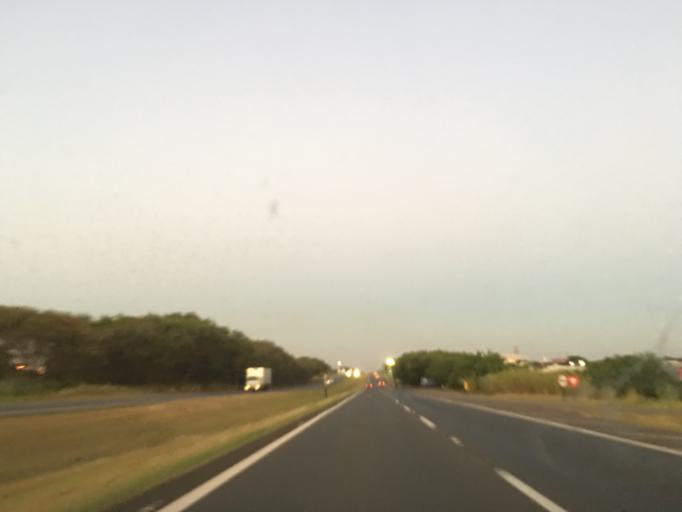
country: BR
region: Sao Paulo
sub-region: Piracicaba
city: Piracicaba
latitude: -22.7219
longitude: -47.6045
